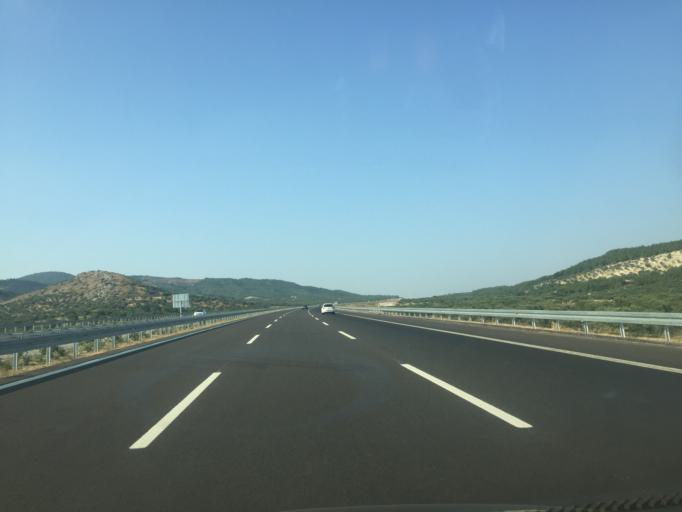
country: TR
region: Manisa
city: Zeytinliova
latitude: 38.9856
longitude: 27.7319
